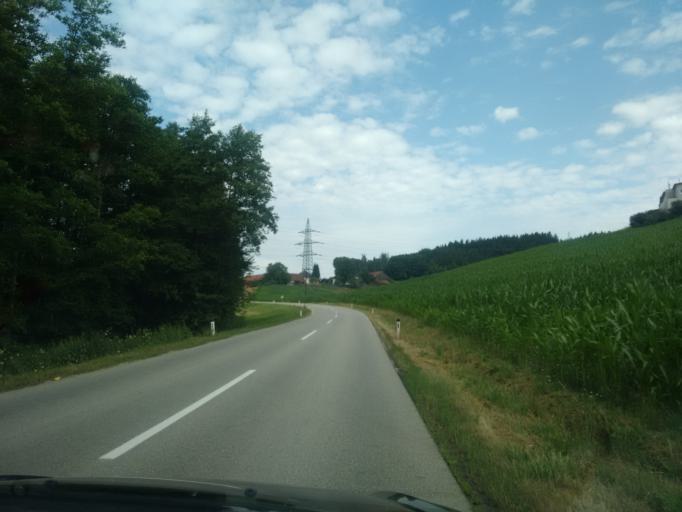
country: AT
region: Upper Austria
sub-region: Politischer Bezirk Grieskirchen
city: Grieskirchen
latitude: 48.1997
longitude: 13.8367
